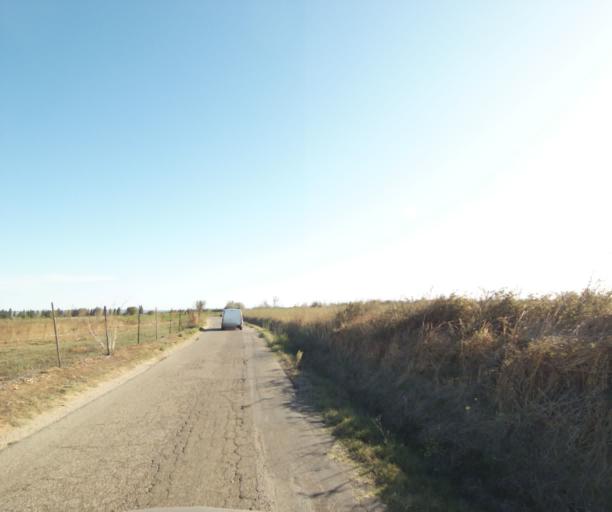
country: FR
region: Languedoc-Roussillon
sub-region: Departement du Gard
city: Bouillargues
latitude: 43.8012
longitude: 4.4488
